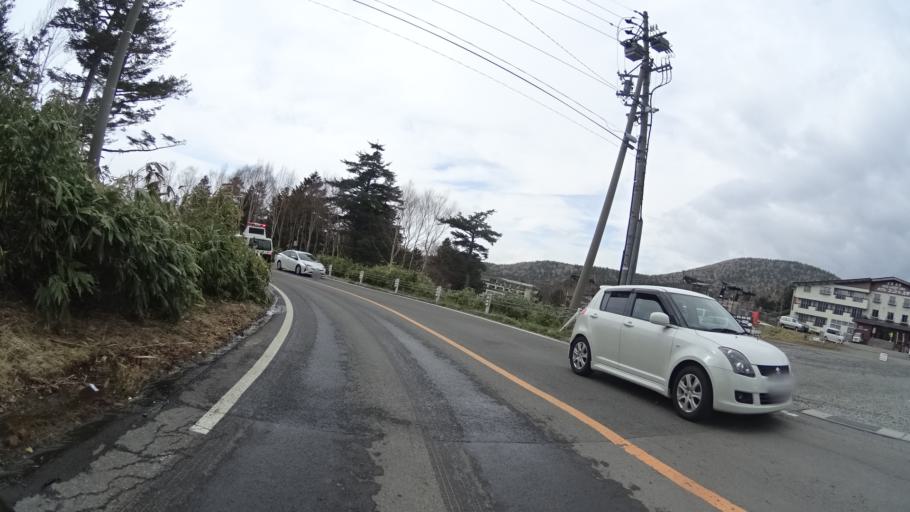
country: JP
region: Nagano
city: Nakano
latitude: 36.6771
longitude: 138.5099
